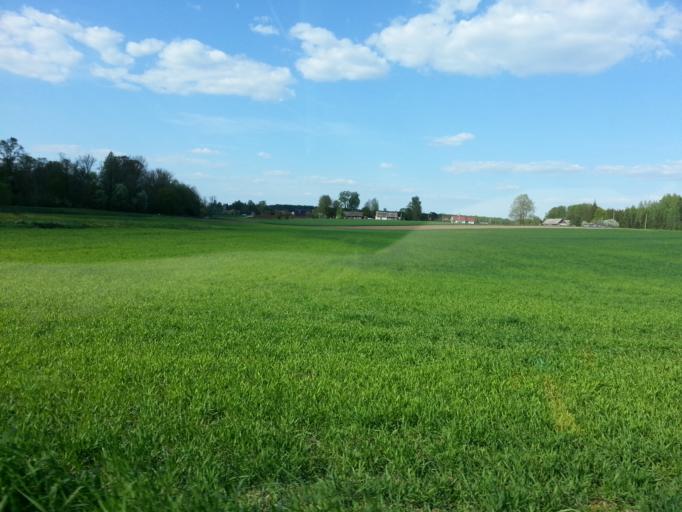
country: LT
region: Panevezys
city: Pasvalys
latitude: 56.0349
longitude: 24.3640
